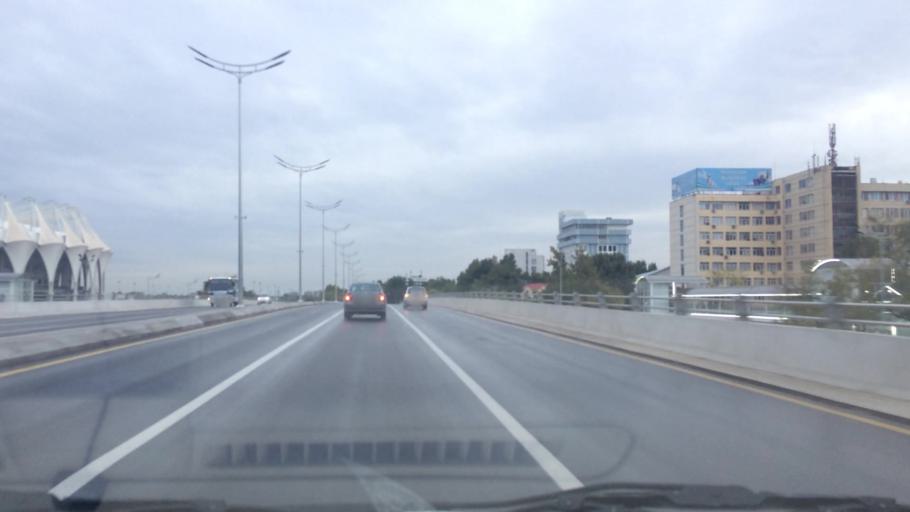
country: UZ
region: Toshkent Shahri
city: Tashkent
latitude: 41.2828
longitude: 69.2128
